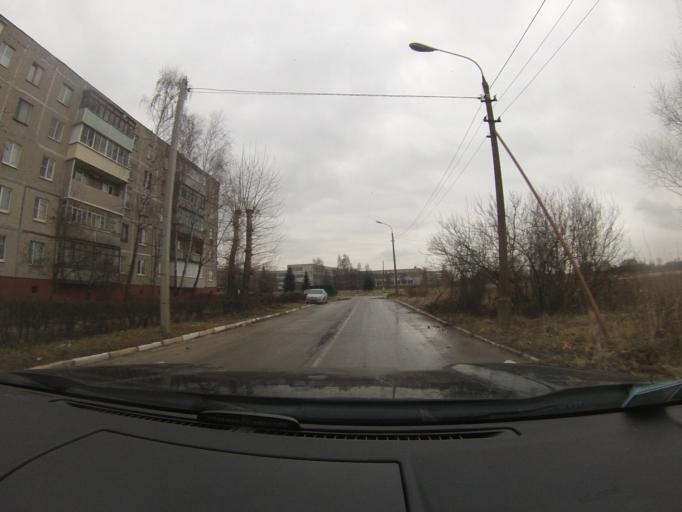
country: RU
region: Moskovskaya
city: Lopatinskiy
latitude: 55.3397
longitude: 38.7118
